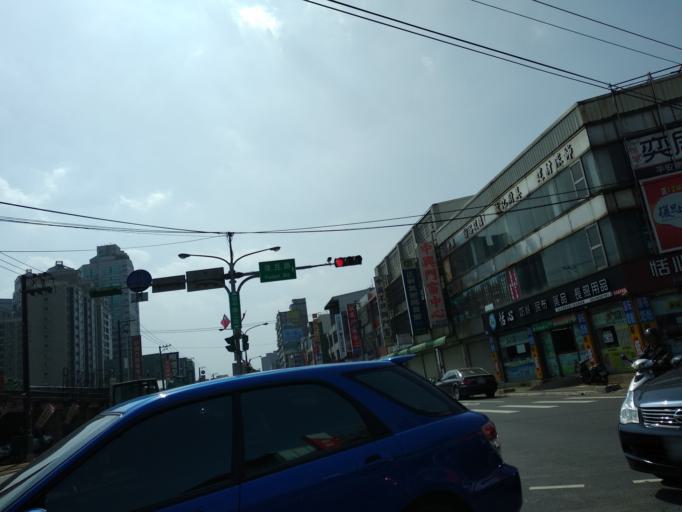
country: TW
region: Taiwan
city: Taoyuan City
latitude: 24.9472
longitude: 121.2103
